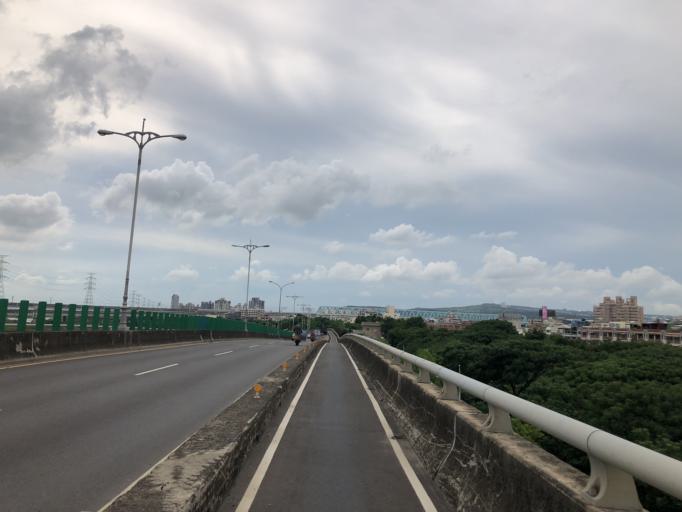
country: TW
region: Taiwan
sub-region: Changhua
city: Chang-hua
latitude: 24.1006
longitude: 120.6237
